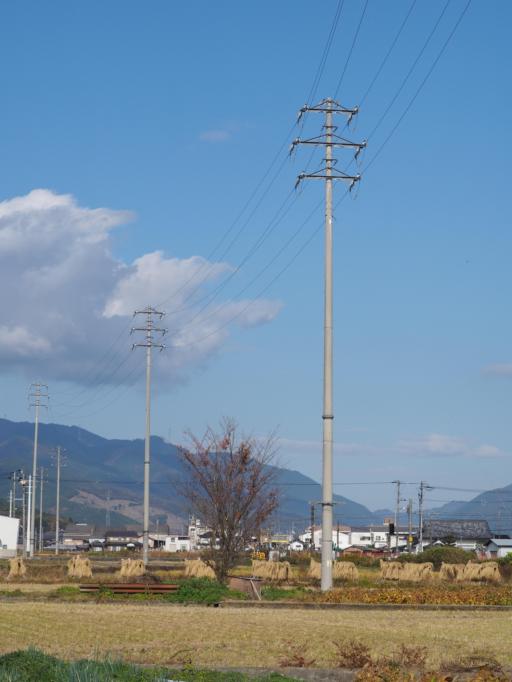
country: JP
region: Hyogo
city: Yamazakicho-nakabirose
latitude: 35.0159
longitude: 134.7530
